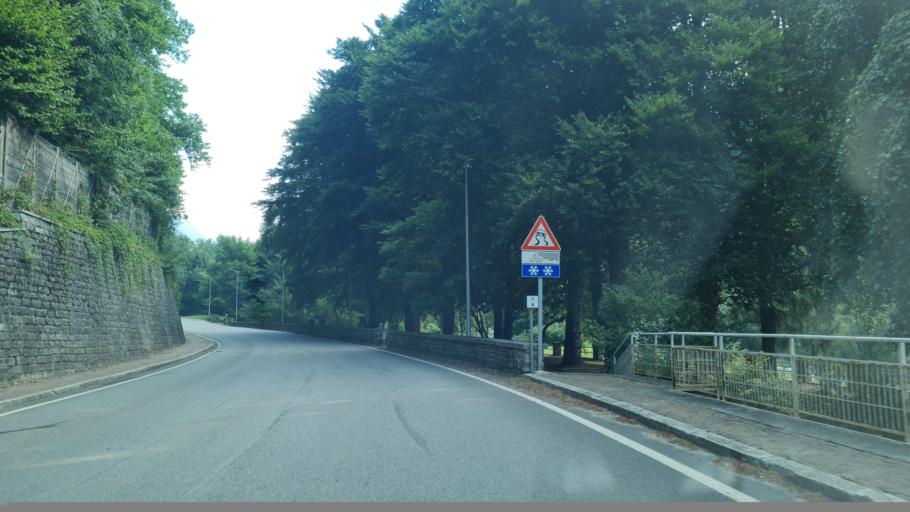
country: IT
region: Piedmont
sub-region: Provincia Verbano-Cusio-Ossola
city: Crodo
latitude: 46.2170
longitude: 8.3230
